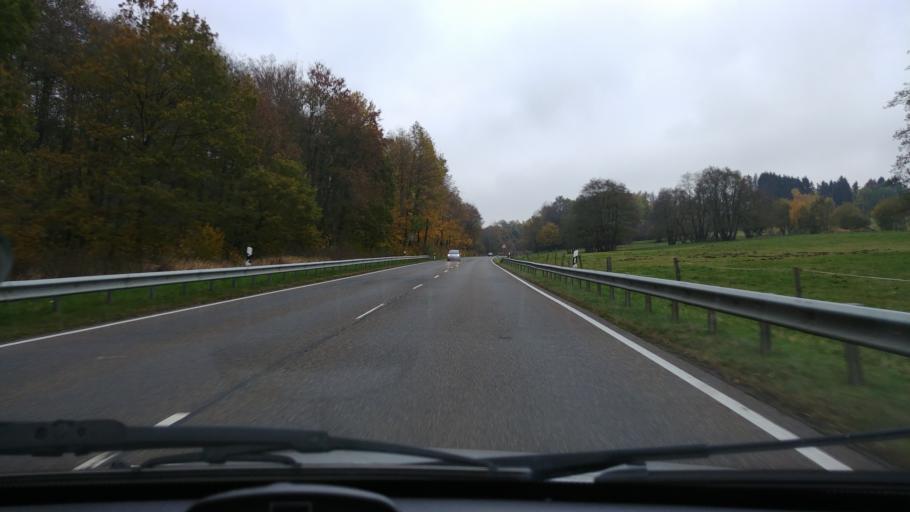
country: DE
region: Rheinland-Pfalz
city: Enspel
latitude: 50.6139
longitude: 7.8826
